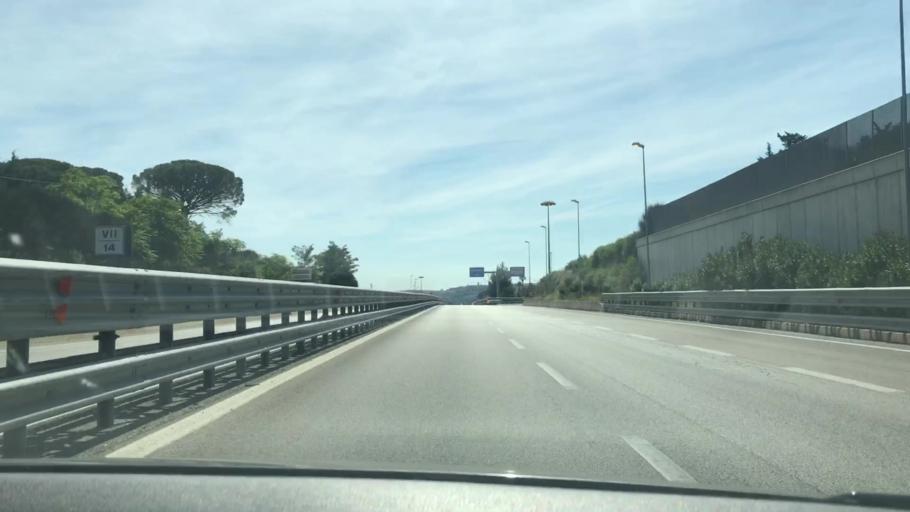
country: IT
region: Basilicate
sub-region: Provincia di Matera
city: Matera
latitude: 40.7034
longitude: 16.5852
